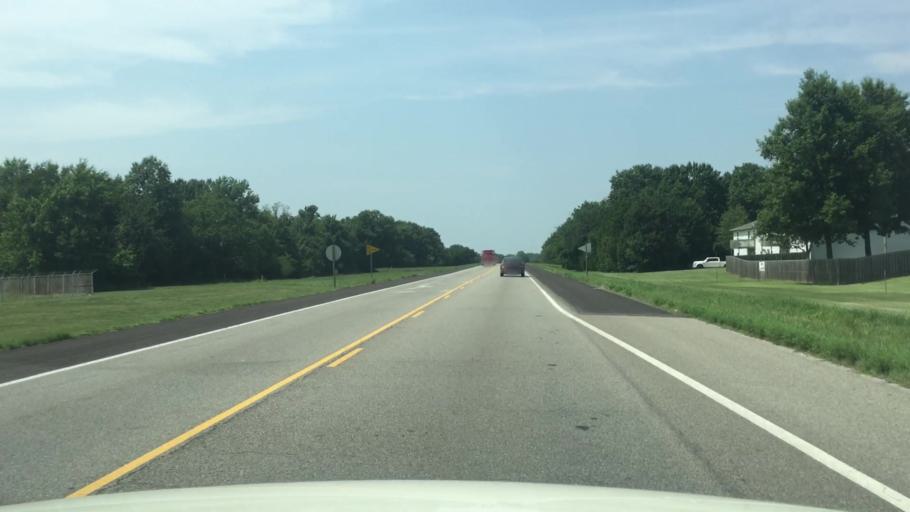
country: US
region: Kansas
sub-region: Crawford County
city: Pittsburg
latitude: 37.3877
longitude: -94.7116
